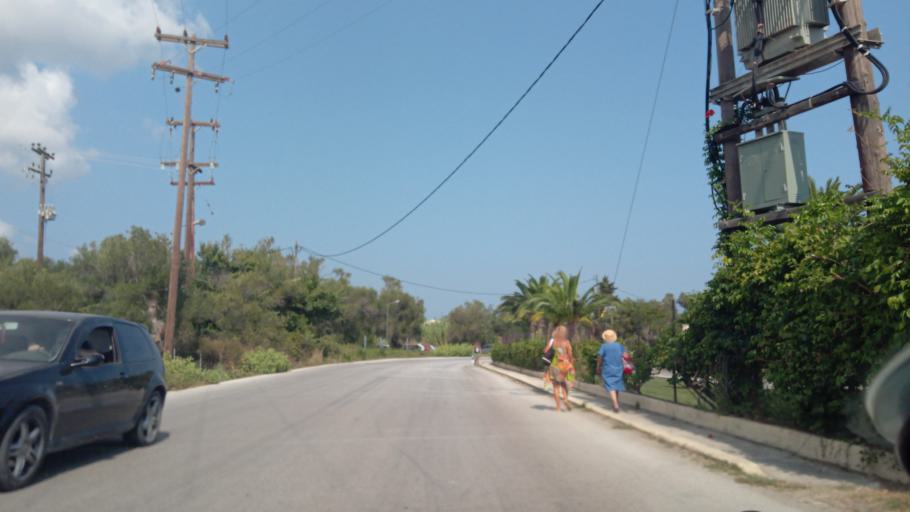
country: GR
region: Ionian Islands
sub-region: Nomos Kerkyras
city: Lefkimmi
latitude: 39.4028
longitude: 20.0972
